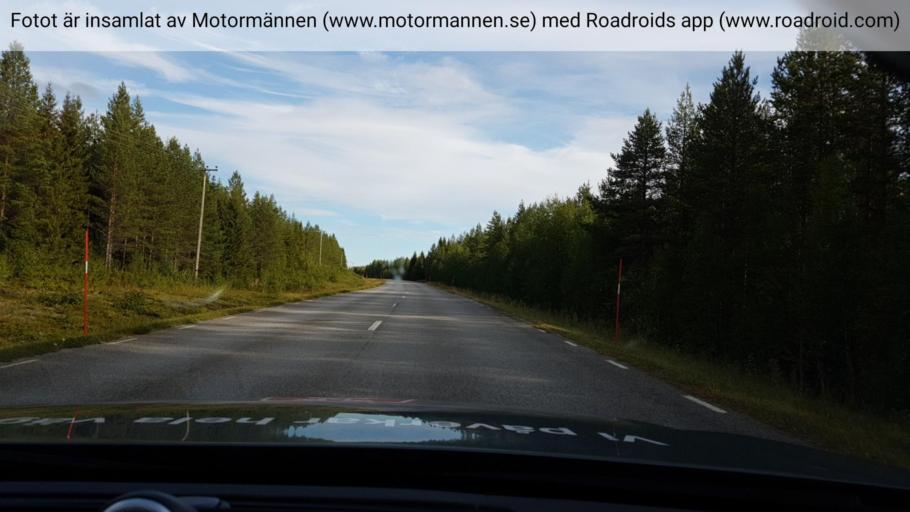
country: SE
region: Jaemtland
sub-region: Stroemsunds Kommun
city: Stroemsund
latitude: 64.2846
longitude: 15.3532
